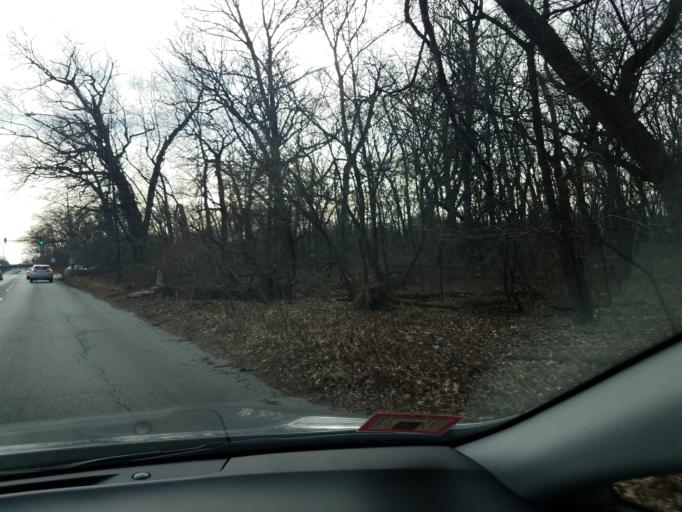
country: US
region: Illinois
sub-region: Cook County
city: Lincolnwood
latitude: 41.9864
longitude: -87.7484
